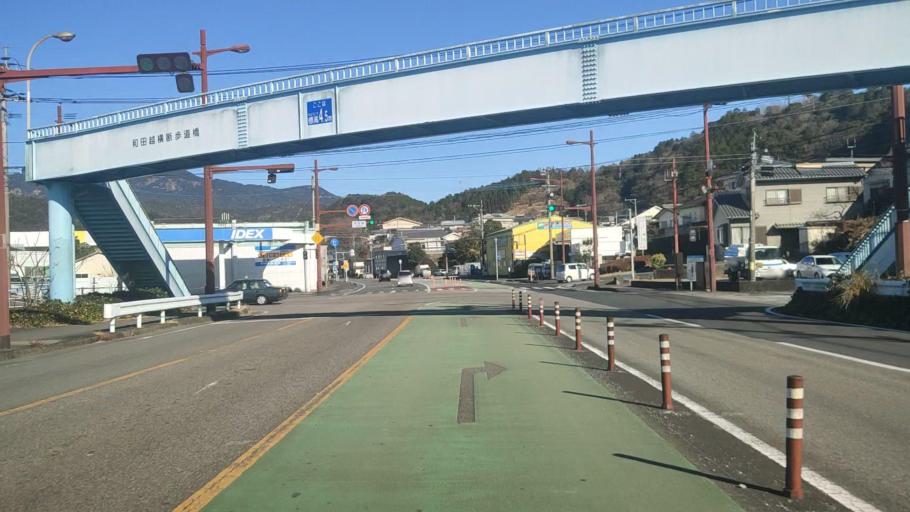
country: JP
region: Miyazaki
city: Nobeoka
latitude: 32.6096
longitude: 131.6834
